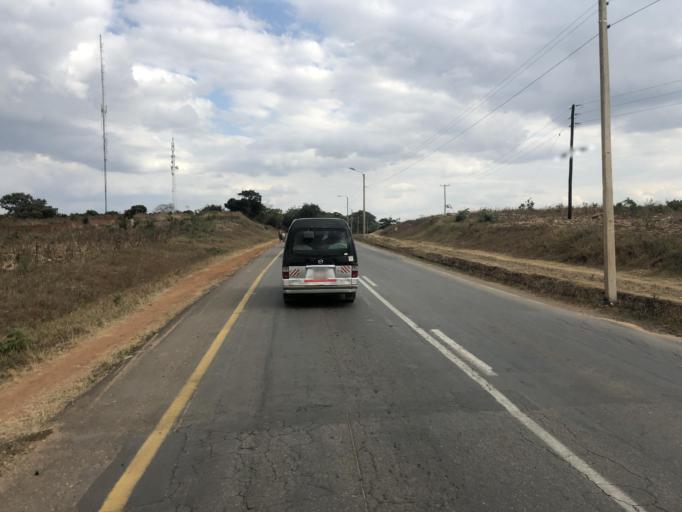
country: MW
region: Central Region
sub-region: Lilongwe District
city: Lilongwe
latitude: -13.8691
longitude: 33.8030
